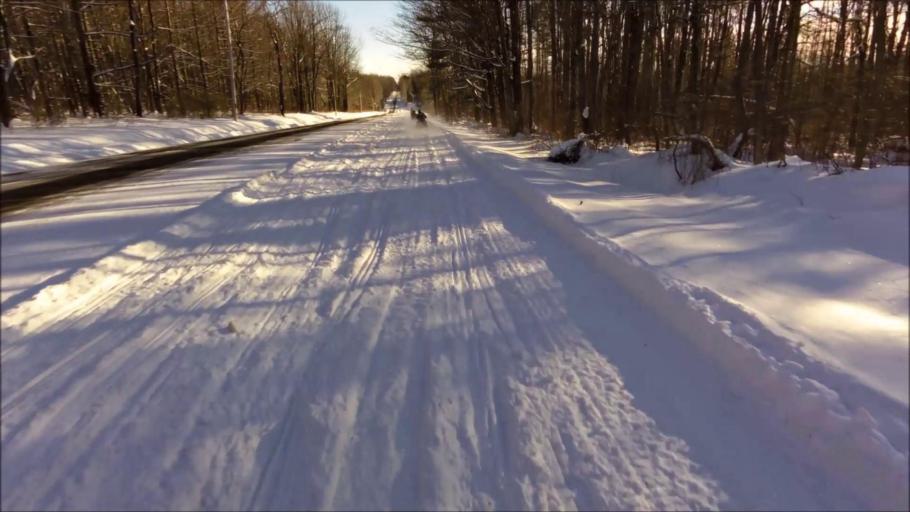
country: US
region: New York
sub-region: Chautauqua County
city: Mayville
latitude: 42.2796
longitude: -79.3972
